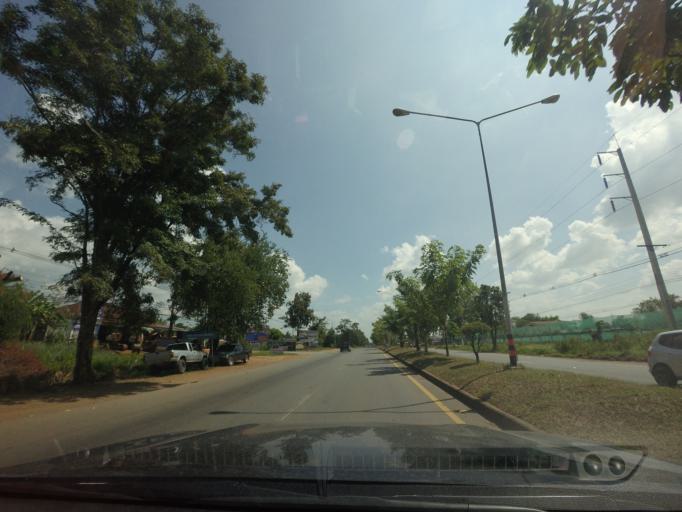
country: TH
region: Phetchabun
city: Nong Phai
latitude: 16.0603
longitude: 101.0738
